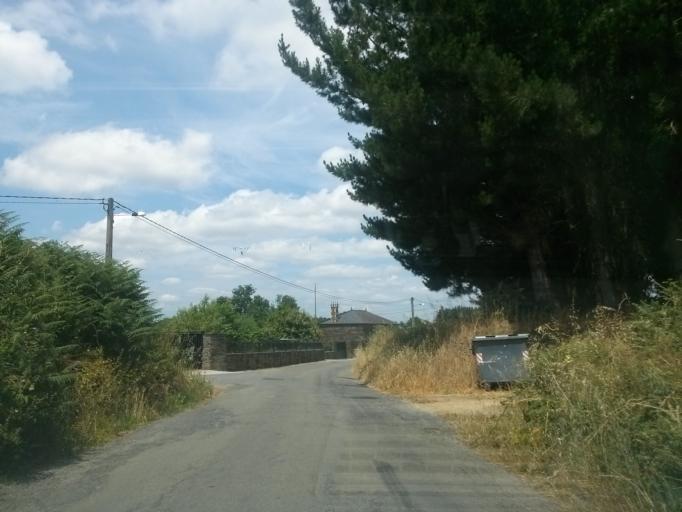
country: ES
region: Galicia
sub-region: Provincia de Lugo
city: Lugo
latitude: 43.0382
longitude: -7.6075
